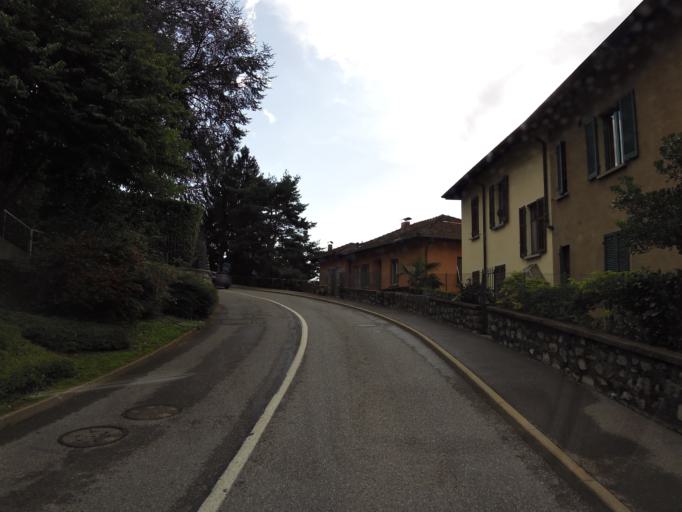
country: CH
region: Ticino
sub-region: Lugano District
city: Viganello
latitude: 46.0151
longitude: 8.9710
